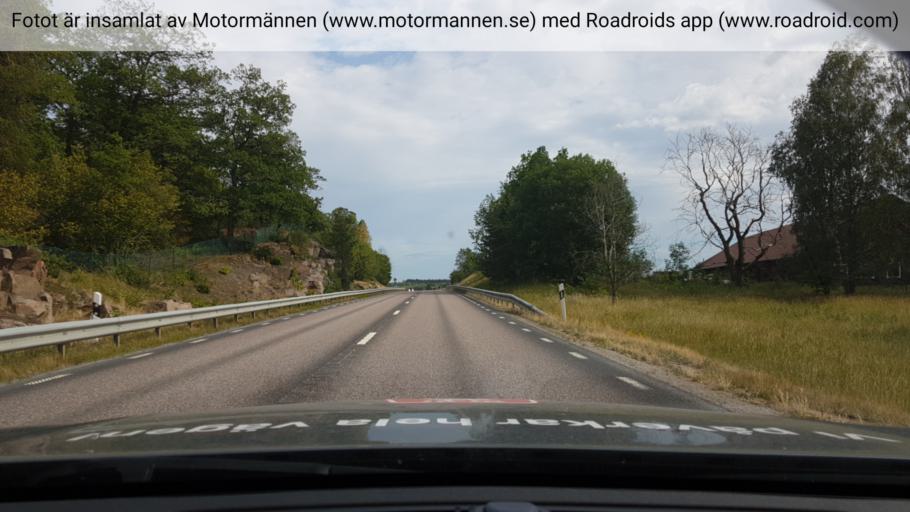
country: SE
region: Uppsala
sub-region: Enkopings Kommun
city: Orsundsbro
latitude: 59.8766
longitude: 17.2884
